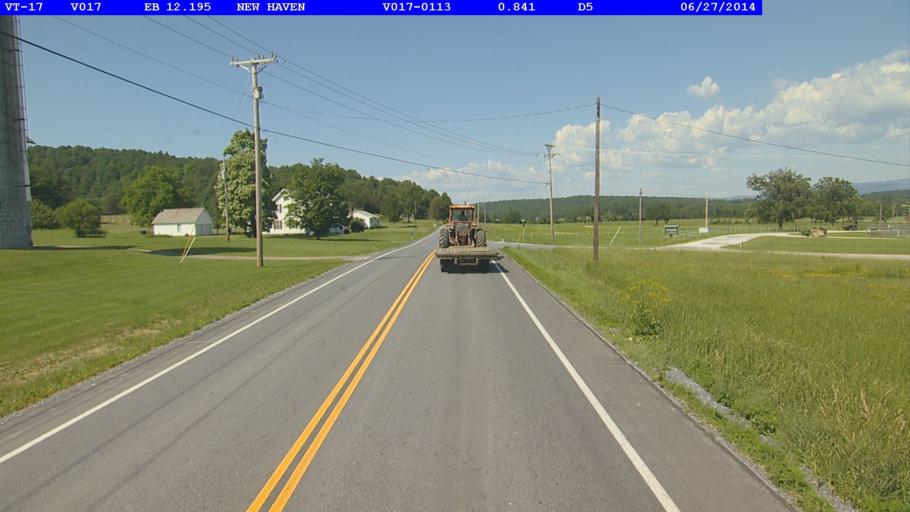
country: US
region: Vermont
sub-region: Addison County
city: Vergennes
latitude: 44.0919
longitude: -73.2331
